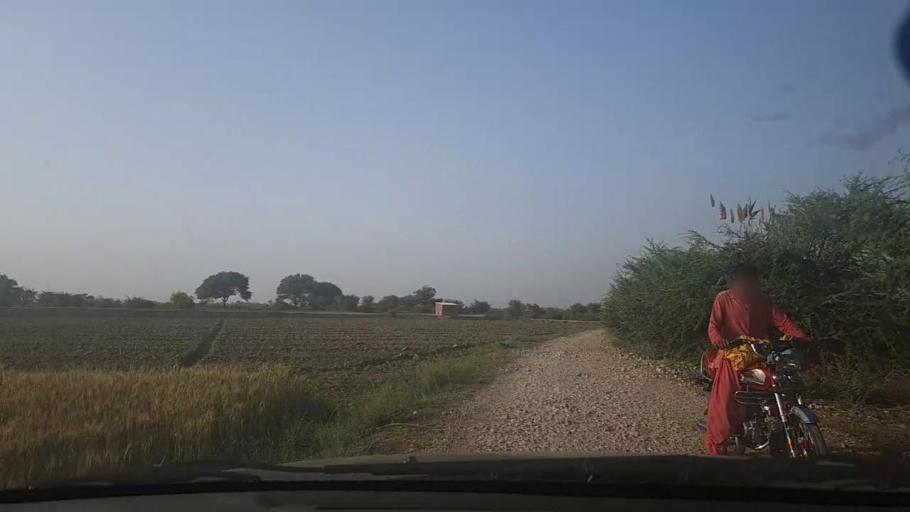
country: PK
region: Sindh
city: Keti Bandar
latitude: 24.2763
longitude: 67.5957
